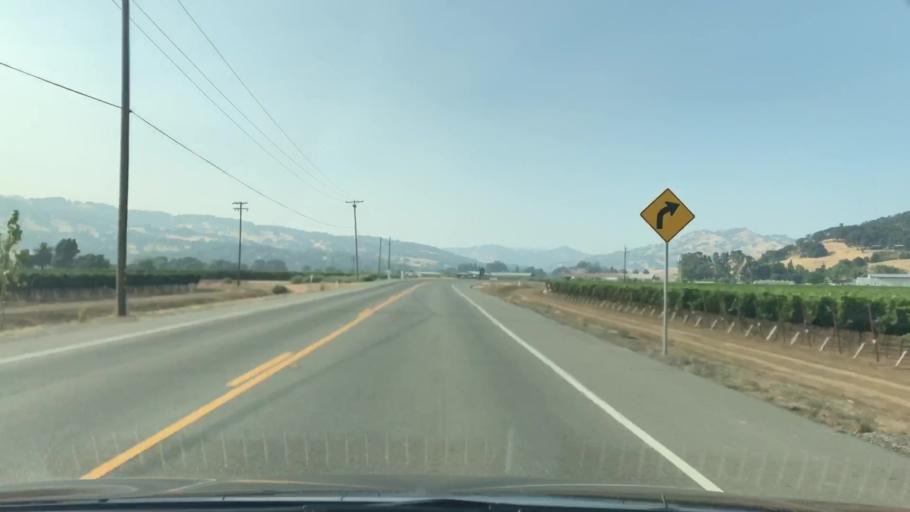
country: US
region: California
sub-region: Solano County
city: Green Valley
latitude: 38.2833
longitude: -122.1175
